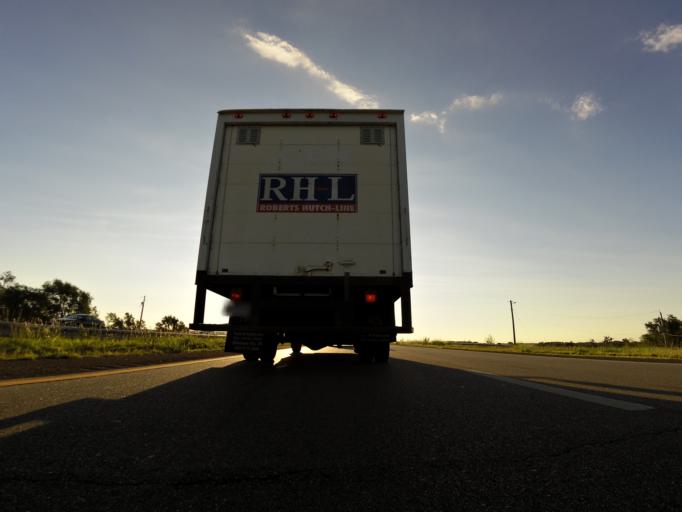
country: US
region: Kansas
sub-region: Sedgwick County
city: Maize
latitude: 37.7596
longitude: -97.4095
